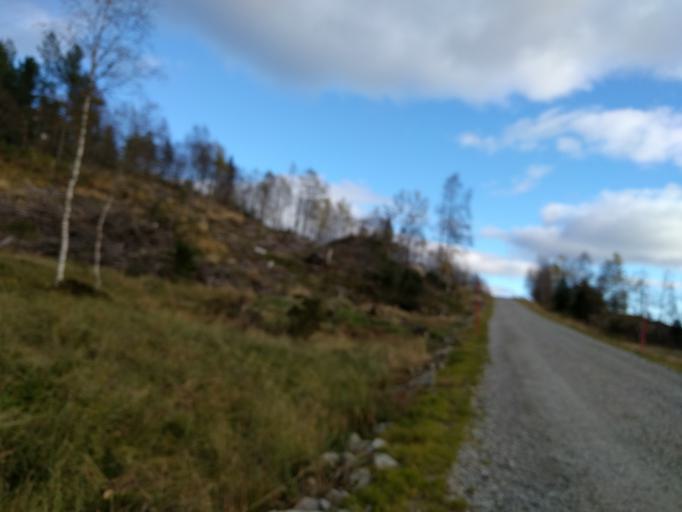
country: NO
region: Aust-Agder
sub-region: Evje og Hornnes
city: Evje
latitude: 58.6536
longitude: 7.9462
